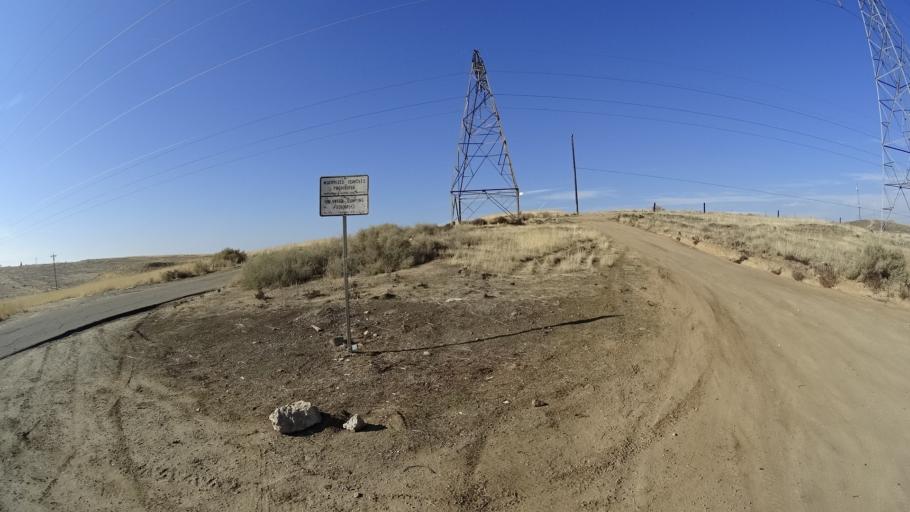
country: US
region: California
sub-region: Kern County
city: Oildale
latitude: 35.4126
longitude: -118.9227
